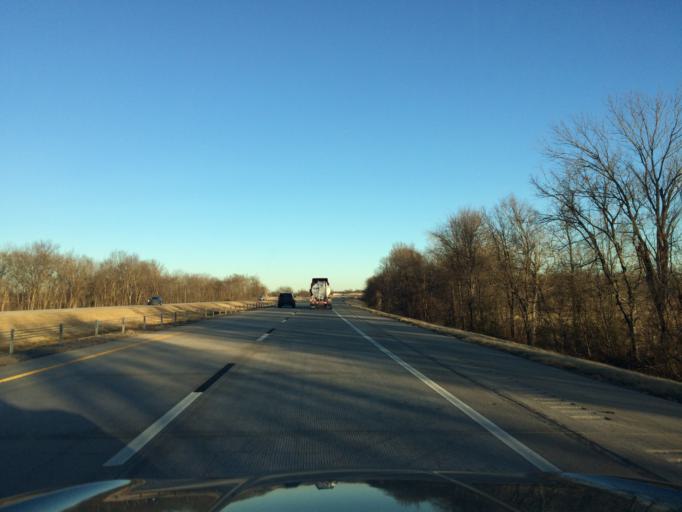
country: US
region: Oklahoma
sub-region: Sequoyah County
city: Sallisaw
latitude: 35.4555
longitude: -94.8544
